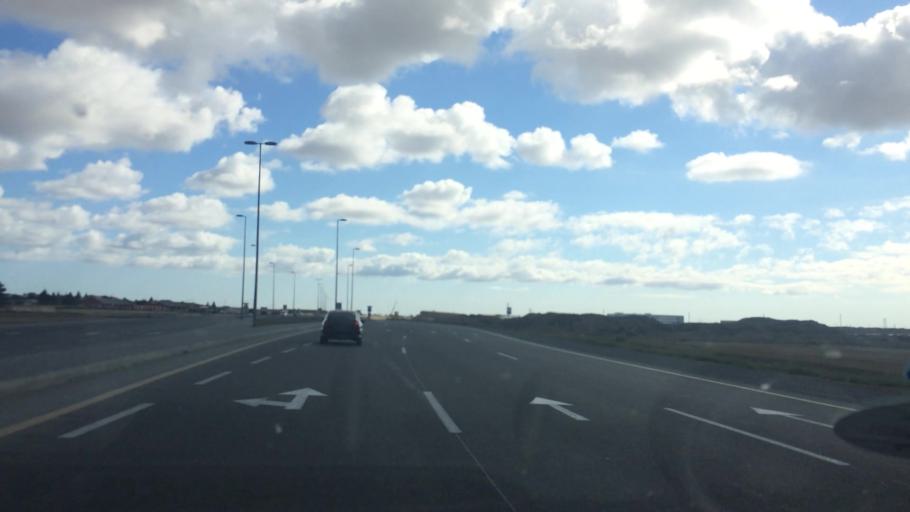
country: AZ
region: Baki
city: Mardakyany
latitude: 40.4585
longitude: 50.1306
